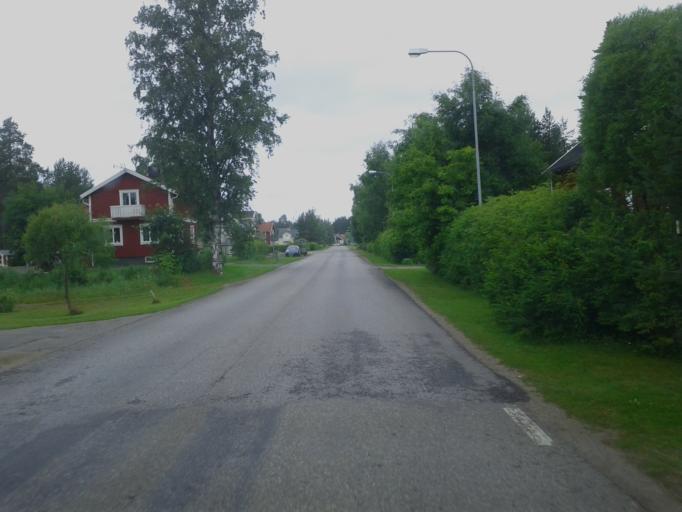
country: SE
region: Vaesterbotten
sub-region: Skelleftea Kommun
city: Kage
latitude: 64.9188
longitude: 20.9521
